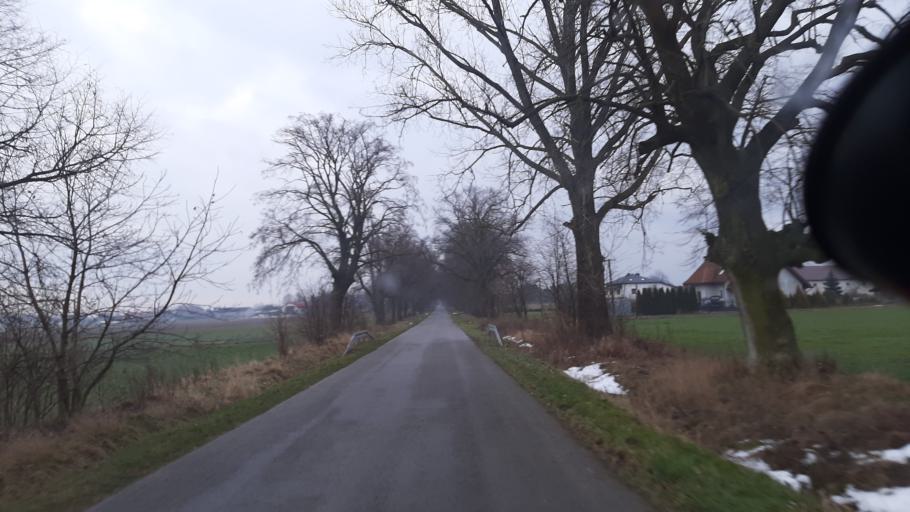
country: PL
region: Lublin Voivodeship
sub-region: Powiat lubelski
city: Lublin
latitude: 51.3431
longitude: 22.5301
